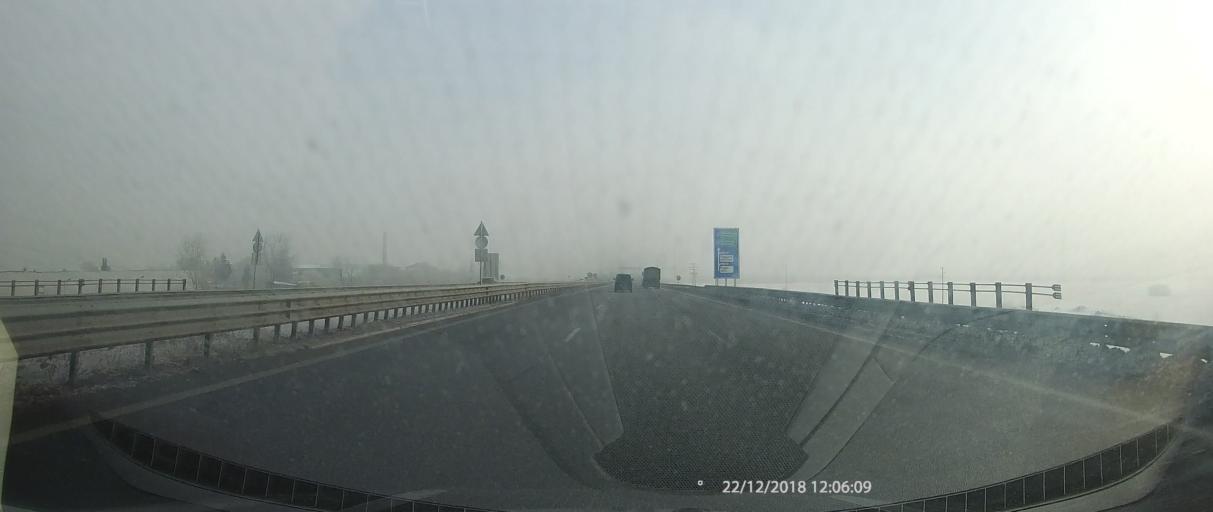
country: BG
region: Sofia-Capital
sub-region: Stolichna Obshtina
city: Sofia
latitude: 42.7562
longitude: 23.3305
